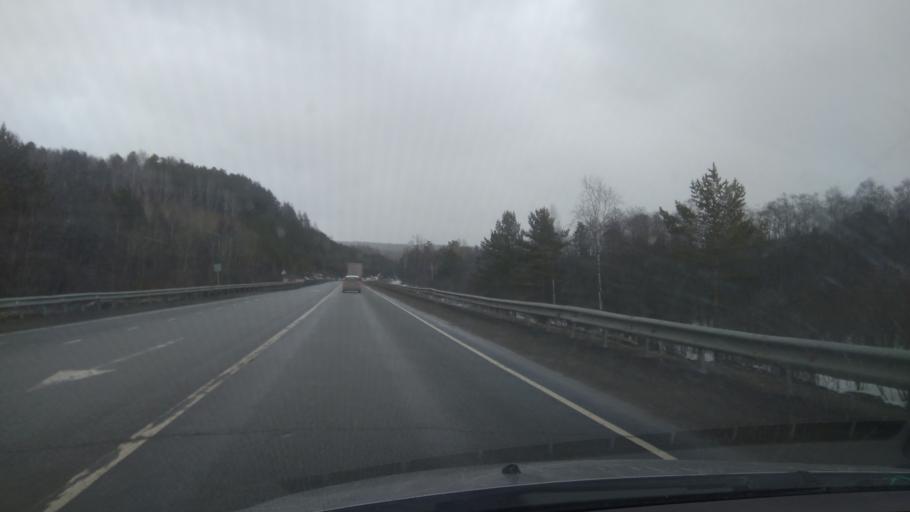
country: RU
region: Sverdlovsk
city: Ufimskiy
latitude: 56.7728
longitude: 58.2151
